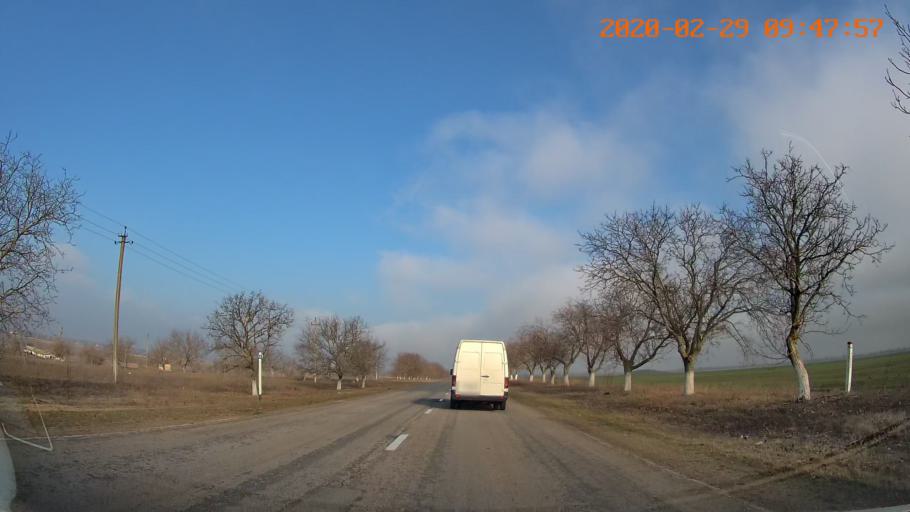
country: MD
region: Telenesti
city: Crasnoe
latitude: 46.6822
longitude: 29.7874
